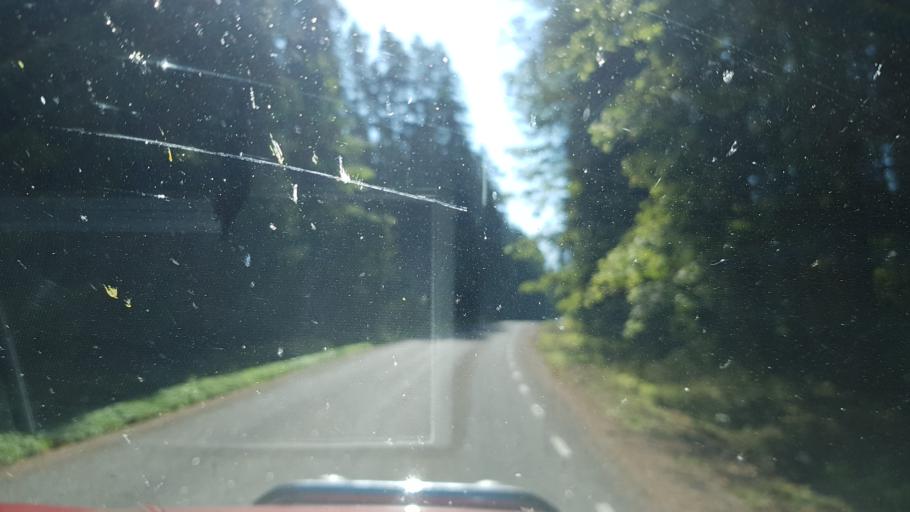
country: EE
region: Tartu
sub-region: UElenurme vald
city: Ulenurme
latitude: 58.3431
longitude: 26.8929
